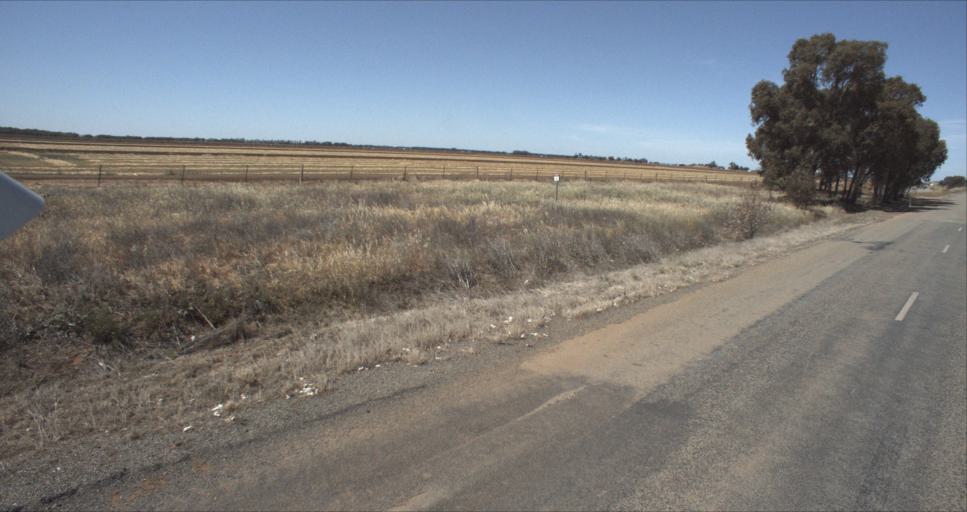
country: AU
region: New South Wales
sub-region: Leeton
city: Leeton
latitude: -34.4933
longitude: 146.2883
